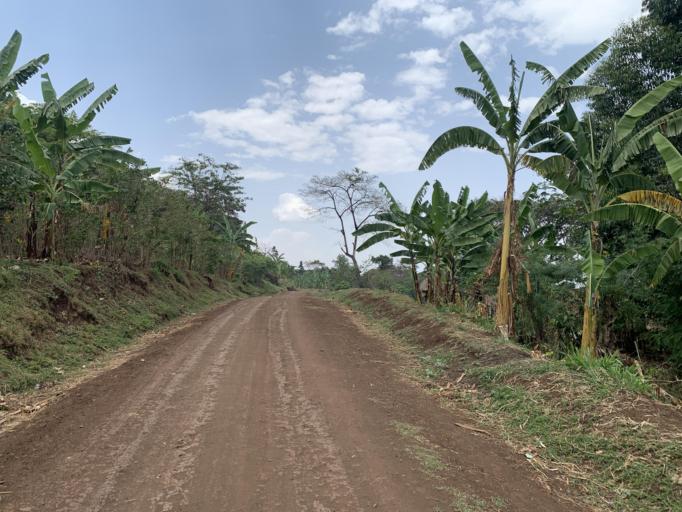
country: UG
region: Eastern Region
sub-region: Sironko District
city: Sironko
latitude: 1.2588
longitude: 34.3079
